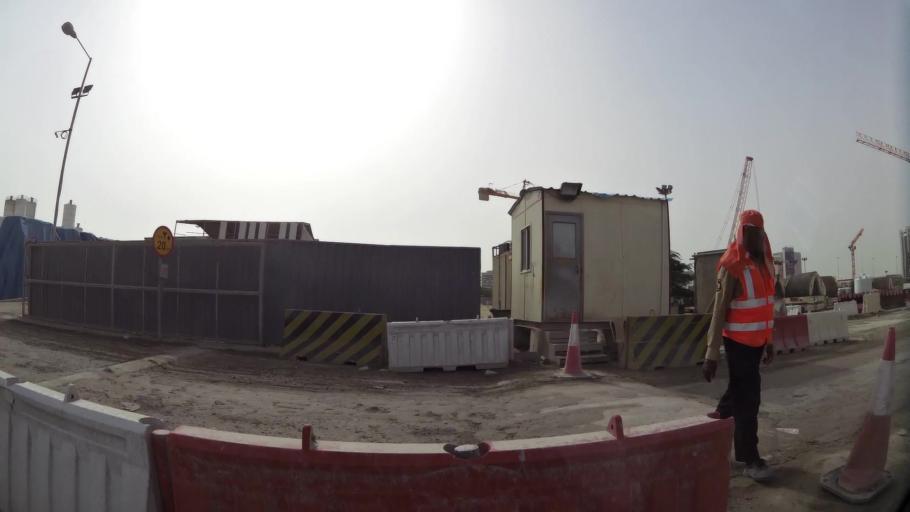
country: QA
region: Baladiyat ad Dawhah
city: Doha
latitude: 25.2723
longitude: 51.5506
